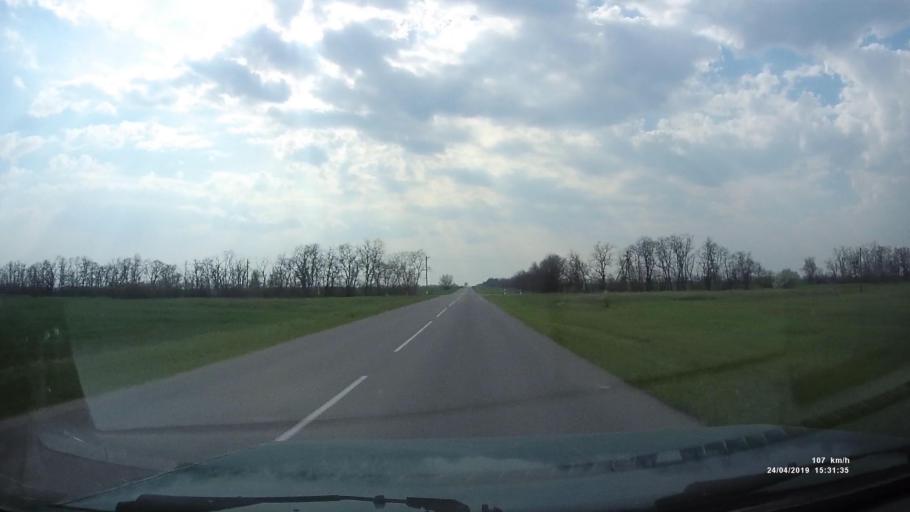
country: RU
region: Rostov
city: Remontnoye
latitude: 46.6002
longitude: 42.9805
